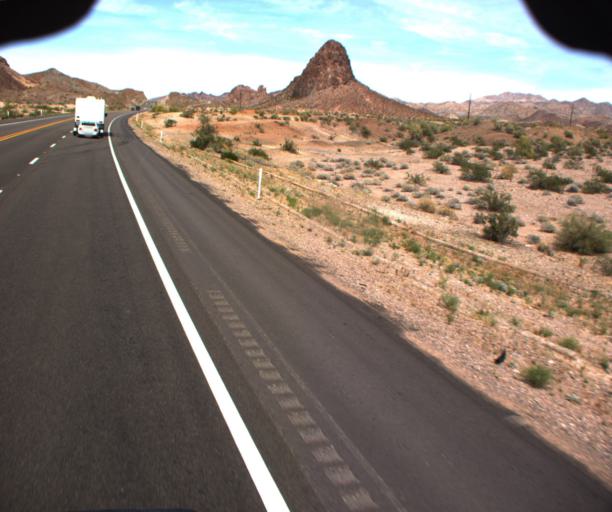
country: US
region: Arizona
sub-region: Mohave County
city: Desert Hills
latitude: 34.6049
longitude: -114.3627
